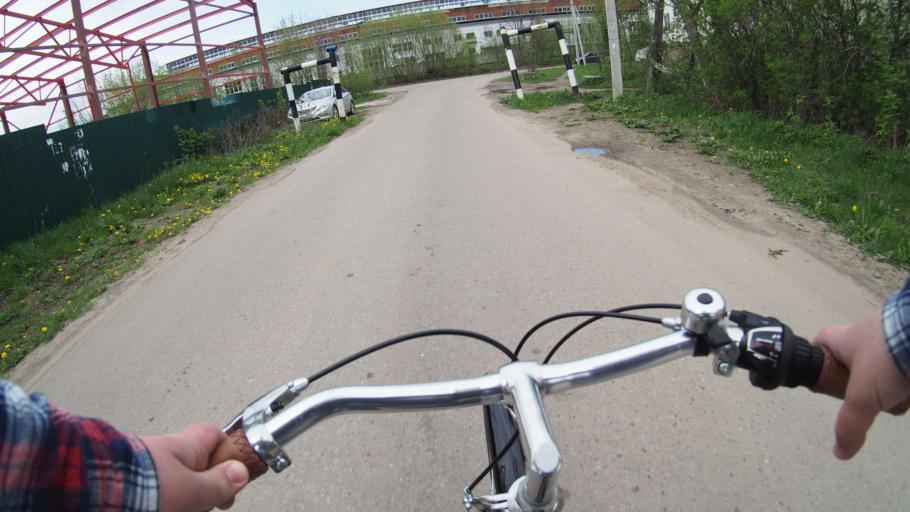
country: RU
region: Moskovskaya
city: Ramenskoye
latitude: 55.5549
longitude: 38.2495
